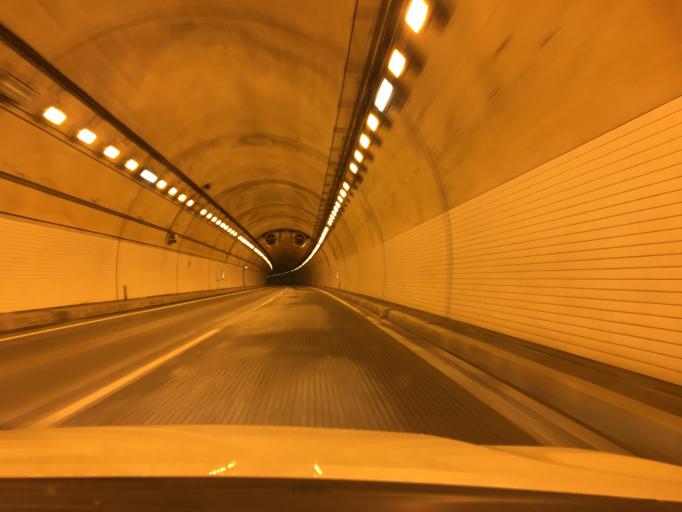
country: JP
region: Yamagata
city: Yamagata-shi
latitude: 38.2307
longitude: 140.4906
